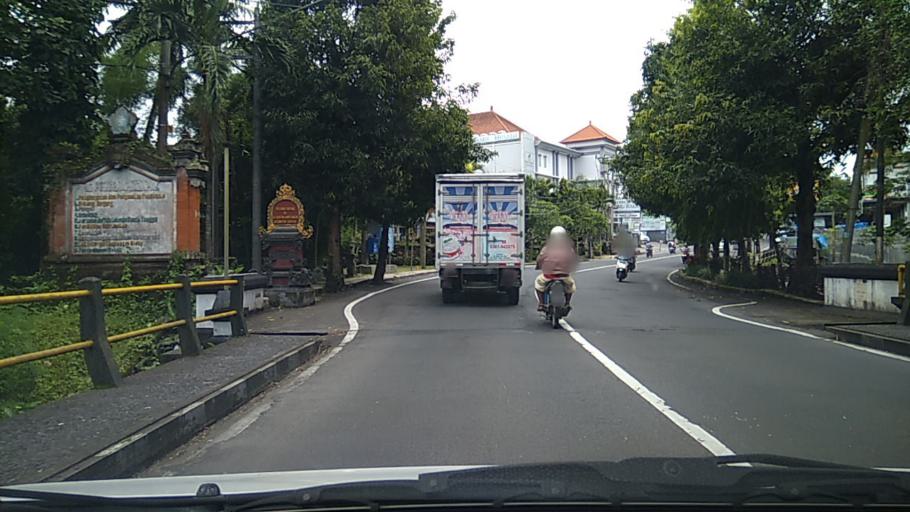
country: ID
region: Bali
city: Banjar Kelodan
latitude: -8.5411
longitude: 115.3339
